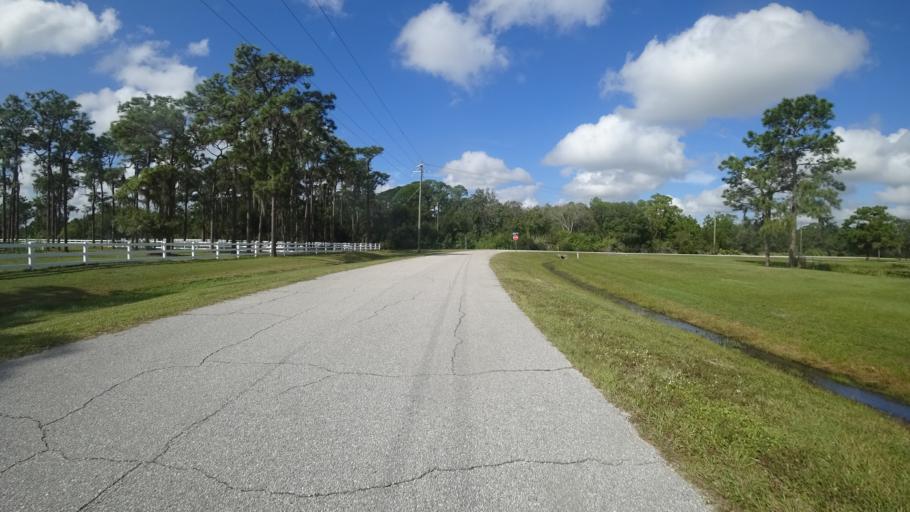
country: US
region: Florida
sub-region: Sarasota County
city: The Meadows
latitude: 27.3984
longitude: -82.3388
